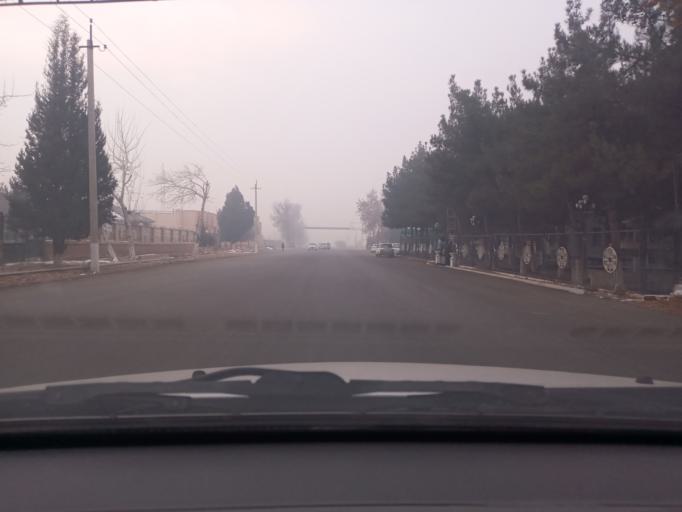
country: UZ
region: Namangan
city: Pop
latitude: 40.8798
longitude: 71.1476
